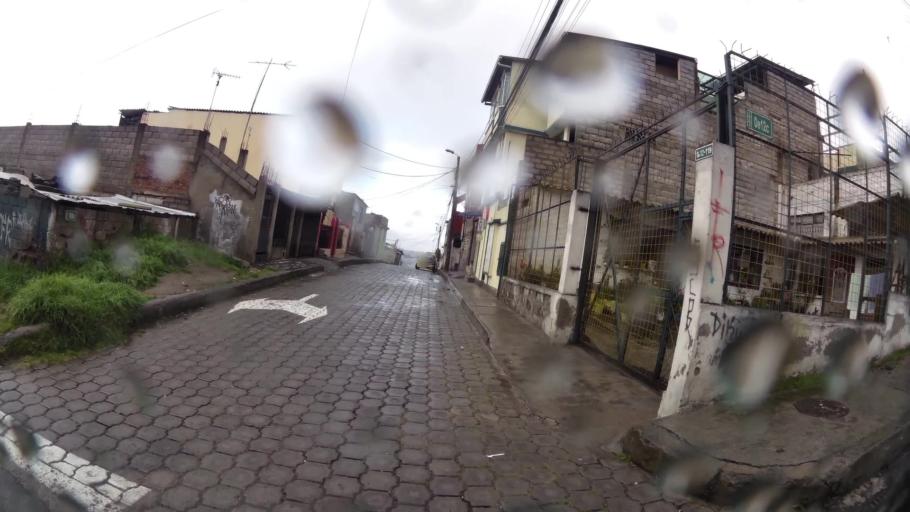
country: EC
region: Pichincha
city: Quito
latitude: -0.0861
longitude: -78.5101
